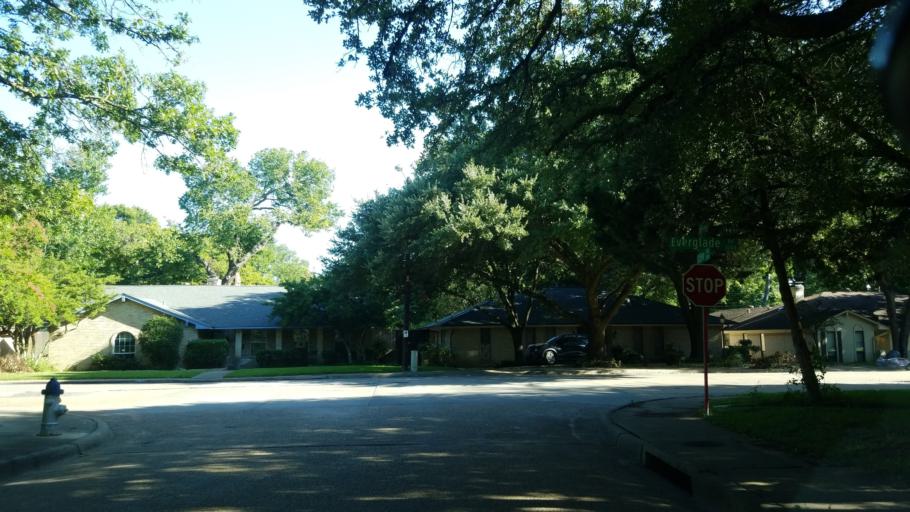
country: US
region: Texas
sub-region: Dallas County
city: Highland Park
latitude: 32.7869
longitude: -96.7093
